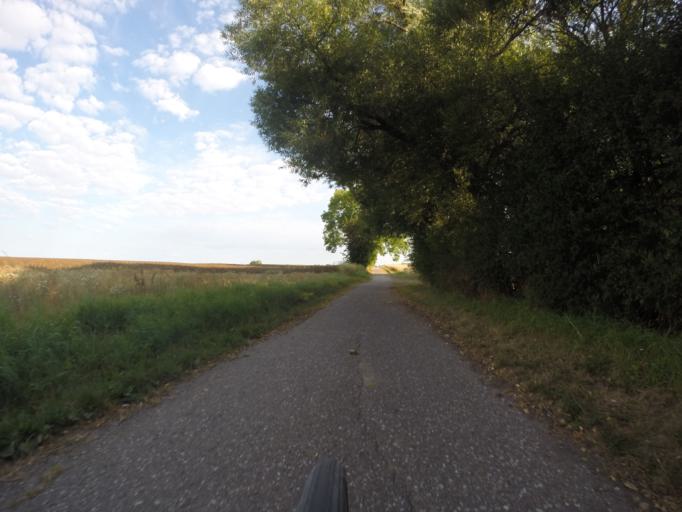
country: DK
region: Capital Region
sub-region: Egedal Kommune
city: Smorumnedre
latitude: 55.6996
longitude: 12.3132
